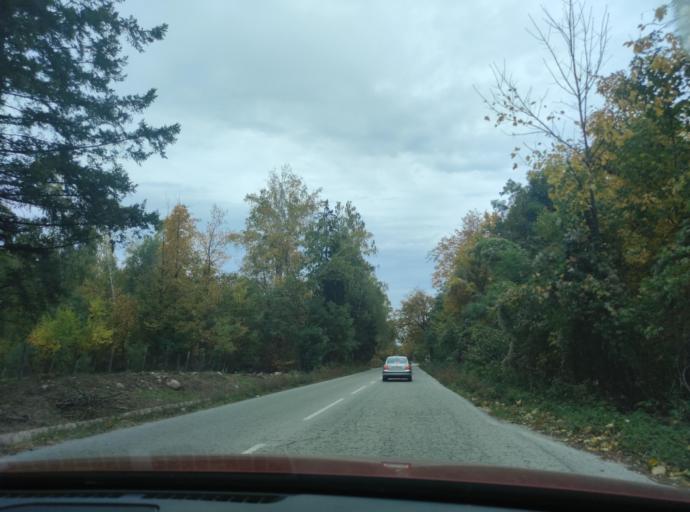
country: BG
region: Montana
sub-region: Obshtina Berkovitsa
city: Berkovitsa
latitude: 43.1812
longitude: 23.1557
